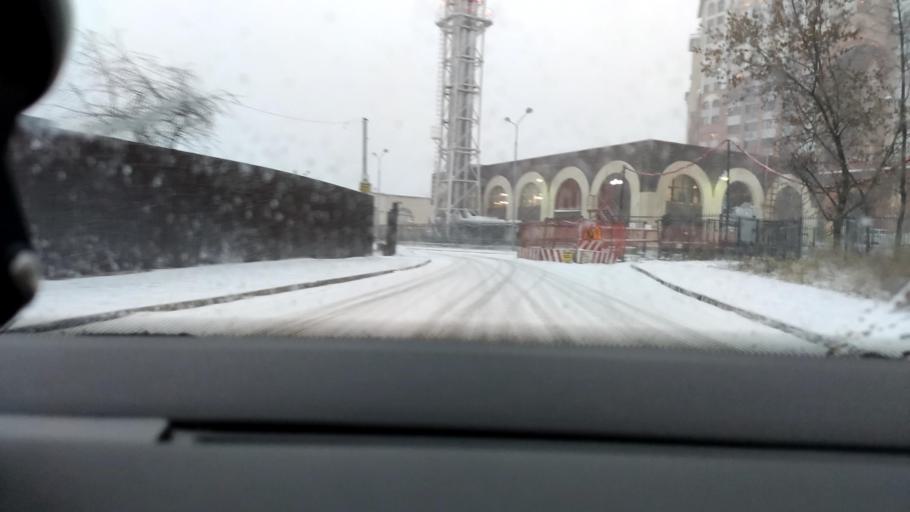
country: RU
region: Moscow
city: Zyablikovo
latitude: 55.5965
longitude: 37.7619
